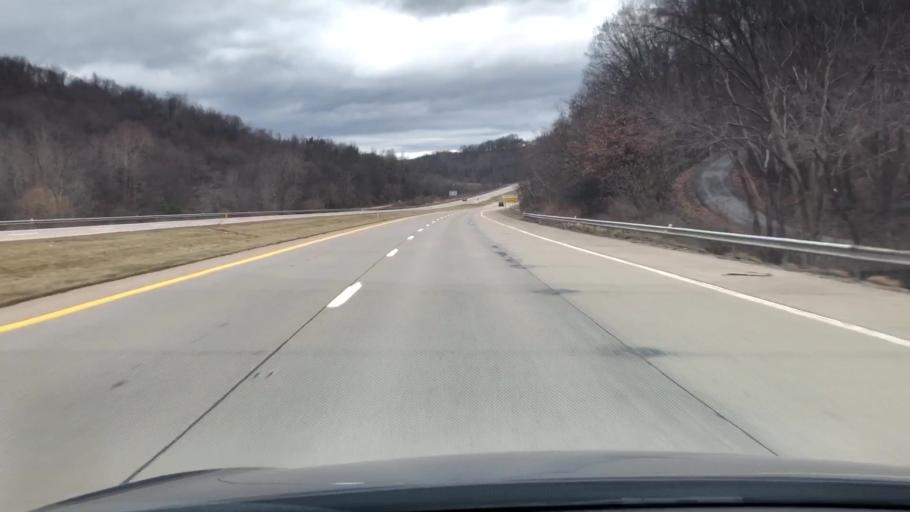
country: US
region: Pennsylvania
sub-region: Westmoreland County
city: New Stanton
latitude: 40.2067
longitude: -79.5859
